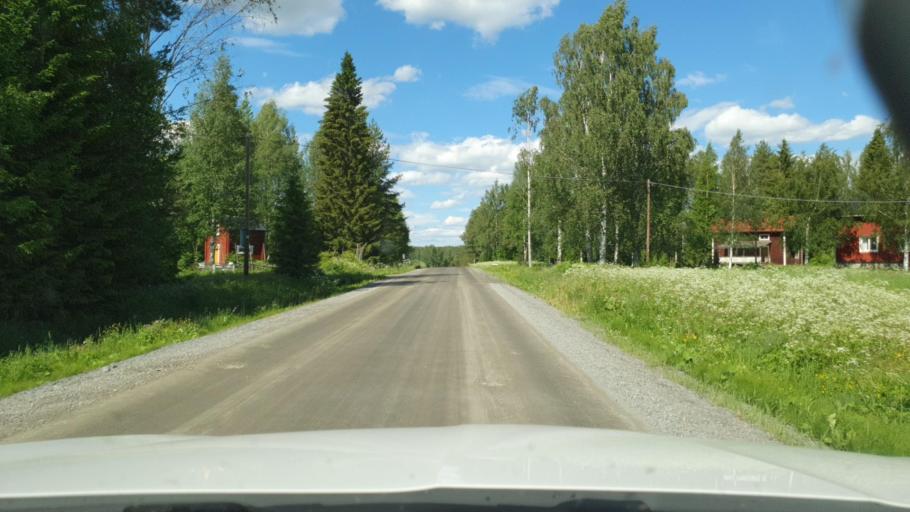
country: SE
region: Vaesterbotten
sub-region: Skelleftea Kommun
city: Forsbacka
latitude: 64.7835
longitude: 20.5135
